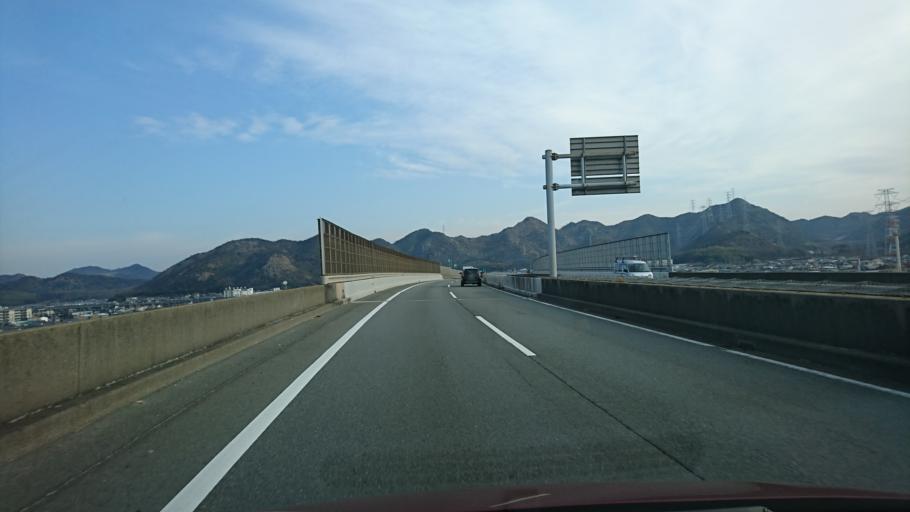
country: JP
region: Hyogo
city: Shirahamacho-usazakiminami
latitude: 34.8103
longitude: 134.7439
